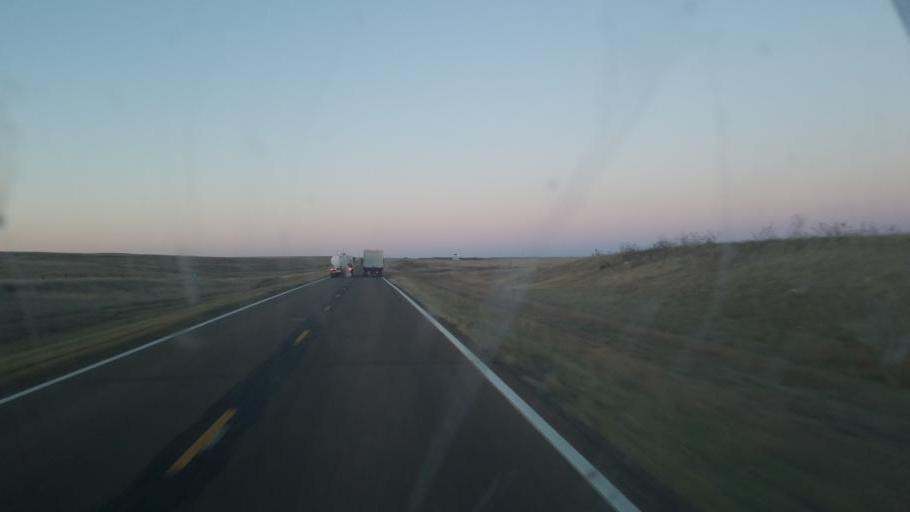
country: US
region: Kansas
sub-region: Wallace County
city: Sharon Springs
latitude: 38.9232
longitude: -101.5639
